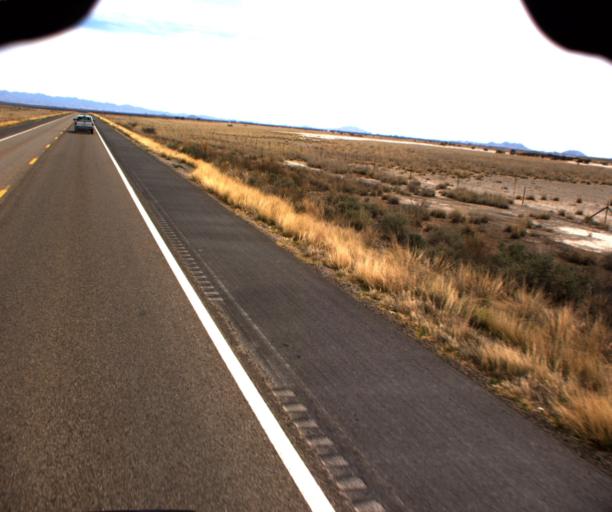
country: US
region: Arizona
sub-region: Cochise County
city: Willcox
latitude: 32.2083
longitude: -109.7753
